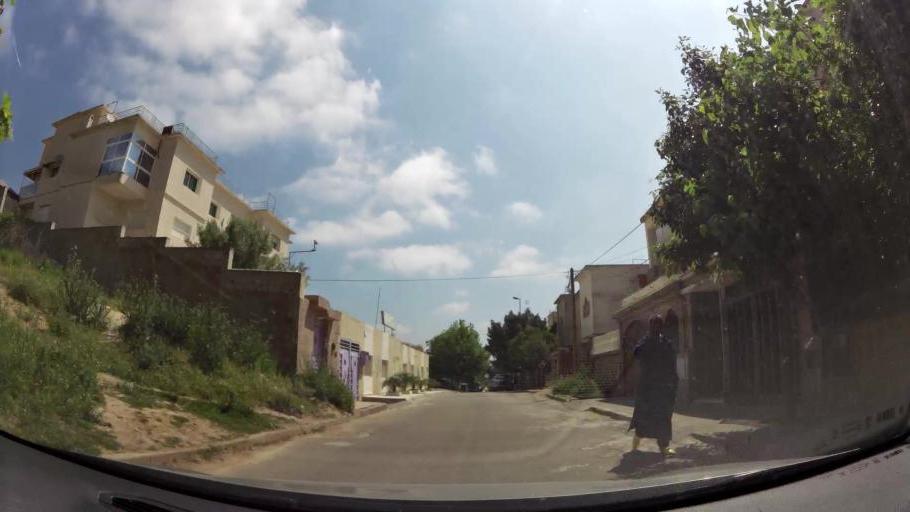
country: MA
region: Fes-Boulemane
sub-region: Fes
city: Fes
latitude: 34.0612
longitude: -5.0384
